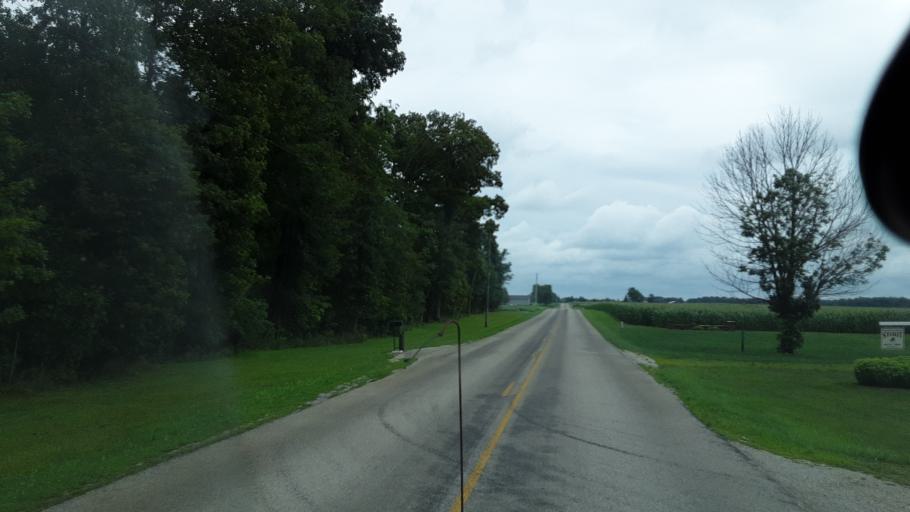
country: US
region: Indiana
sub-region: Jay County
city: Portland
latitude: 40.4821
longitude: -85.0138
